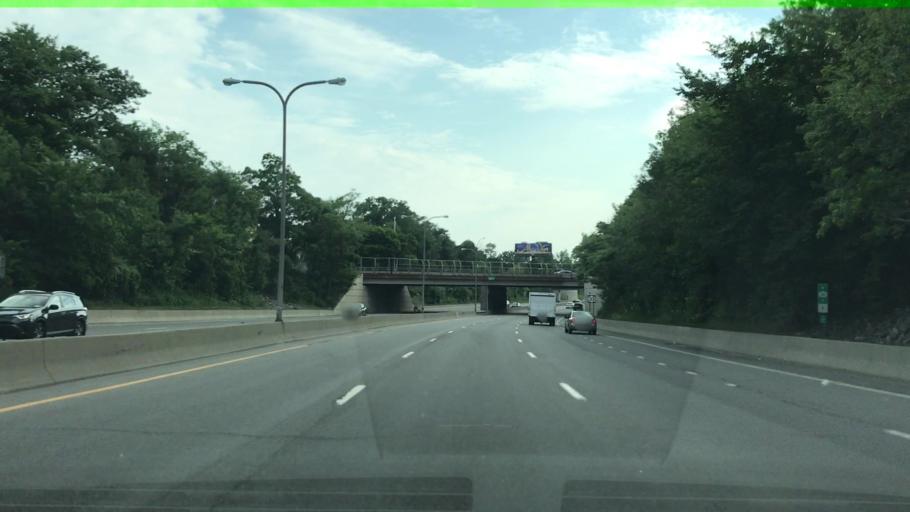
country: US
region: New York
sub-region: Erie County
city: Buffalo
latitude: 42.9012
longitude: -78.8477
